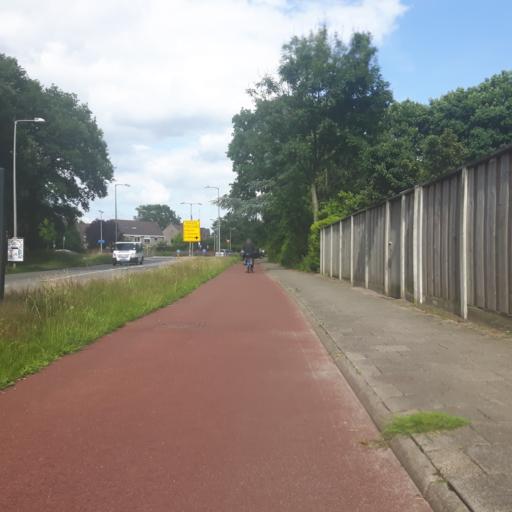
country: NL
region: Overijssel
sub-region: Gemeente Enschede
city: Enschede
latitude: 52.1974
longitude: 6.8953
